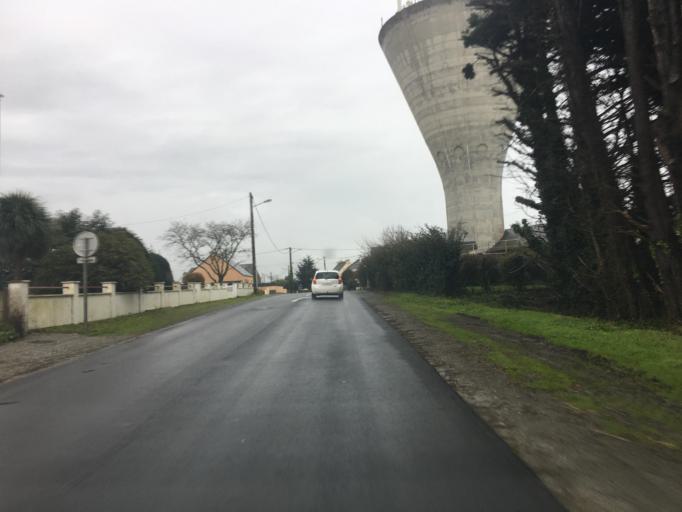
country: FR
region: Pays de la Loire
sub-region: Departement de la Loire-Atlantique
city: La Turballe
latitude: 47.3500
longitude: -2.4876
